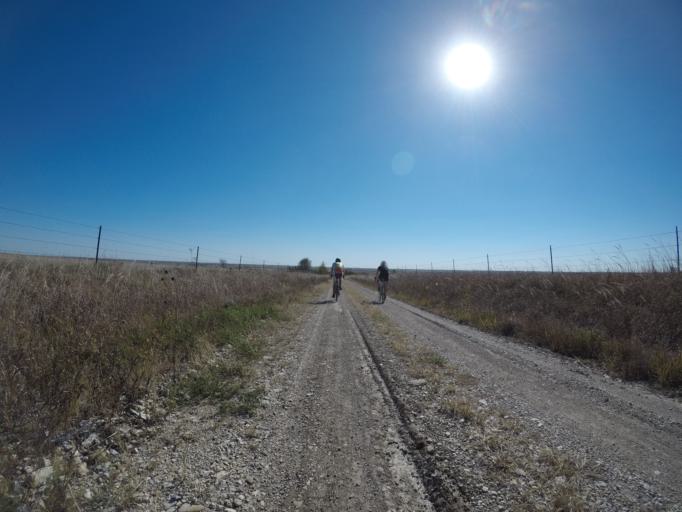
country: US
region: Kansas
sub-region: Wabaunsee County
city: Alma
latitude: 38.9721
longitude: -96.4554
